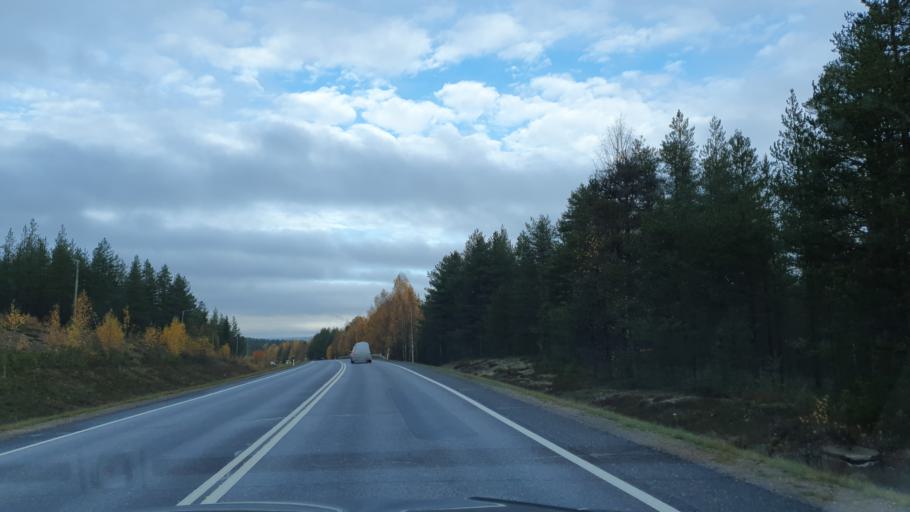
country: FI
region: Lapland
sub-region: Rovaniemi
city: Rovaniemi
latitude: 66.5899
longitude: 25.6102
